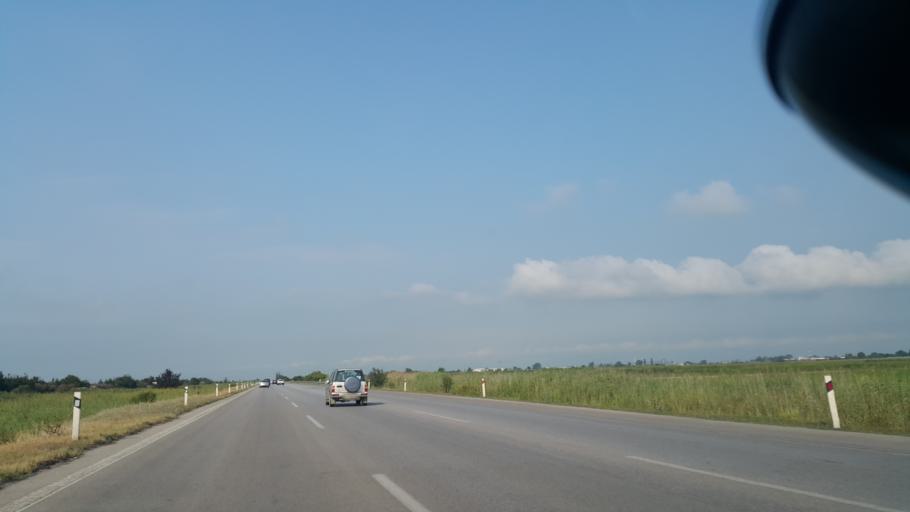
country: GR
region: Central Macedonia
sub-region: Nomos Thessalonikis
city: Sindos
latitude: 40.6351
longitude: 22.7838
